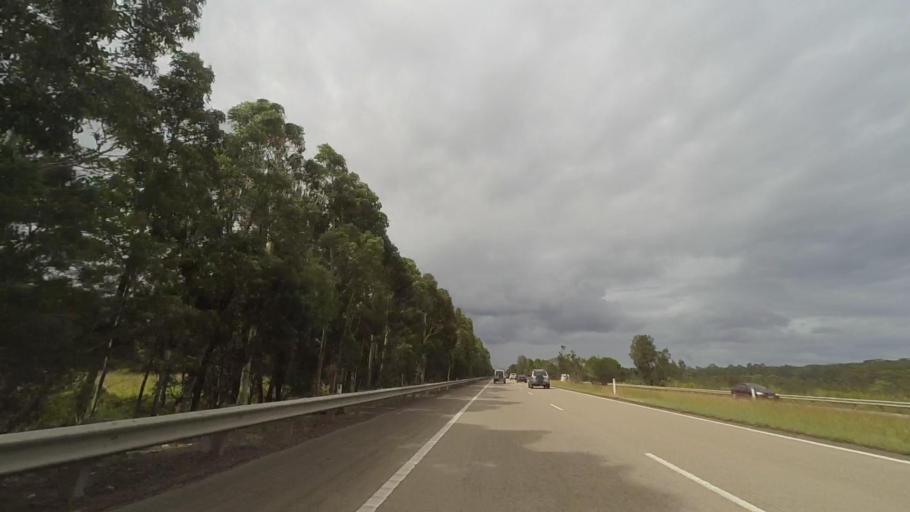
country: AU
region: New South Wales
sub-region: Port Stephens Shire
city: Raymond Terrace
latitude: -32.7302
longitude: 151.7833
